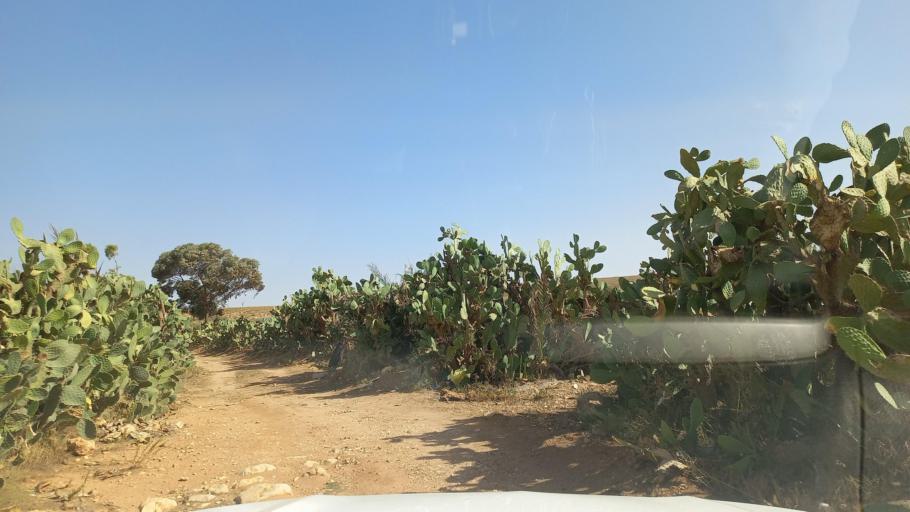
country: TN
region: Al Qasrayn
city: Kasserine
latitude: 35.2086
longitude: 8.9846
